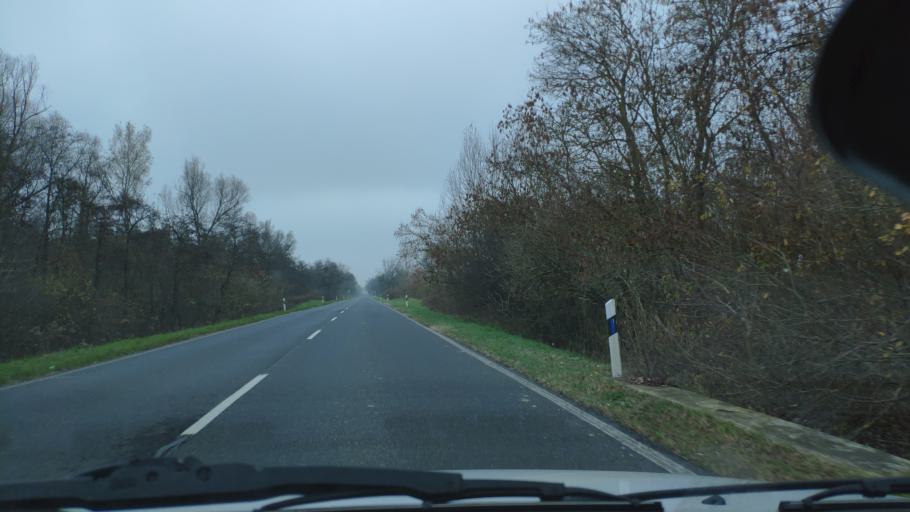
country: HU
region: Somogy
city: Balatonbereny
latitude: 46.6144
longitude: 17.2782
